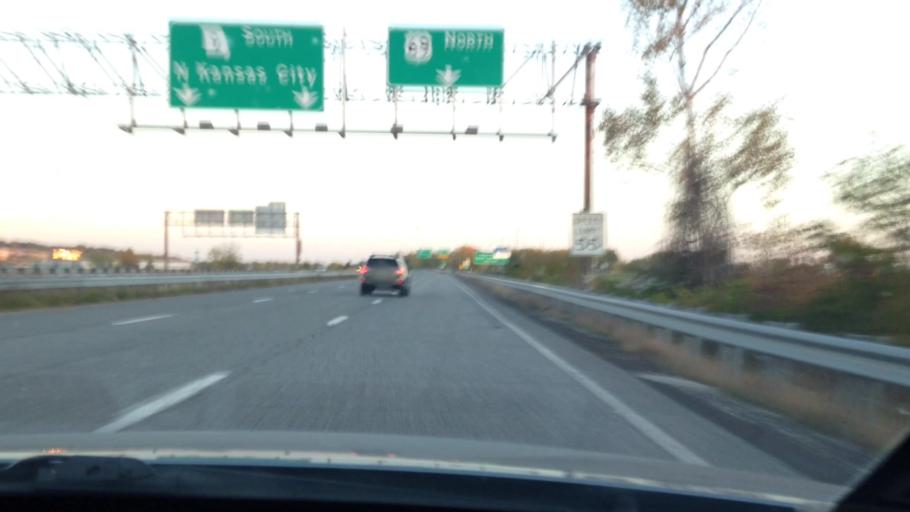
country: US
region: Missouri
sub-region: Platte County
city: Riverside
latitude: 39.1695
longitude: -94.6192
